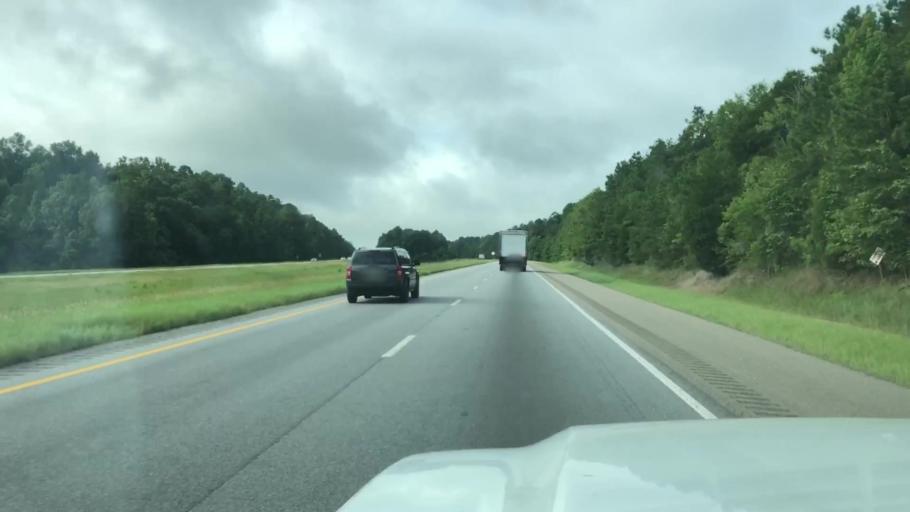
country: US
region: Alabama
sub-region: Lowndes County
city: Fort Deposit
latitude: 32.0084
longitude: -86.5221
